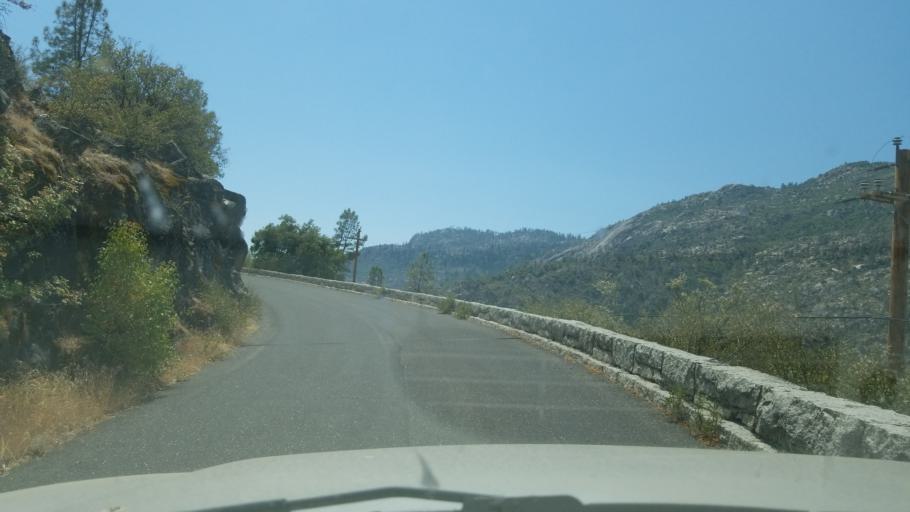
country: US
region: California
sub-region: Mariposa County
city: Yosemite Valley
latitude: 37.9402
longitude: -119.7898
